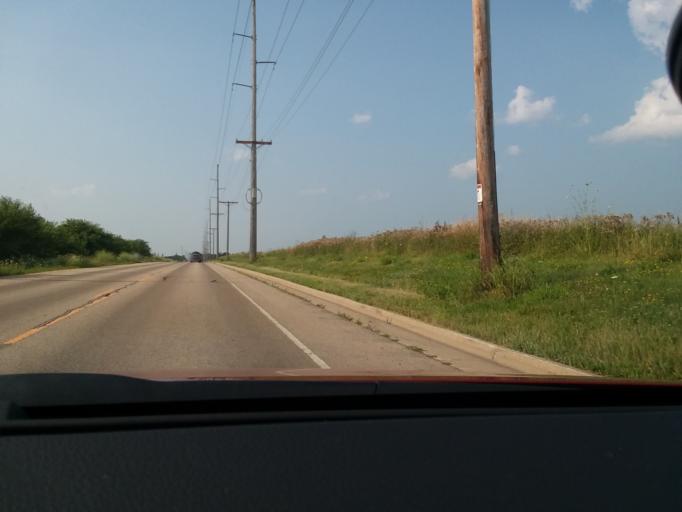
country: US
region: Wisconsin
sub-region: Dane County
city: Cottage Grove
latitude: 43.1147
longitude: -89.2665
